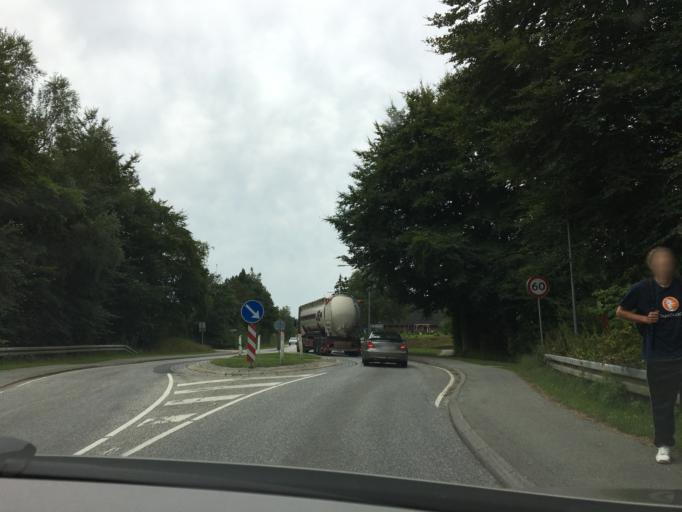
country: DK
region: Central Jutland
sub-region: Viborg Kommune
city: Stoholm
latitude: 56.3864
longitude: 8.9924
